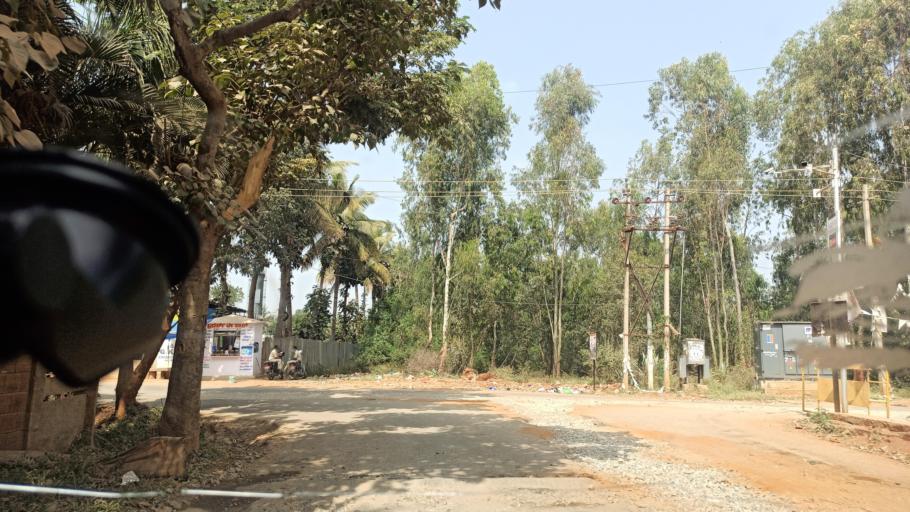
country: IN
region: Karnataka
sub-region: Bangalore Urban
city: Yelahanka
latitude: 13.0978
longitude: 77.6184
